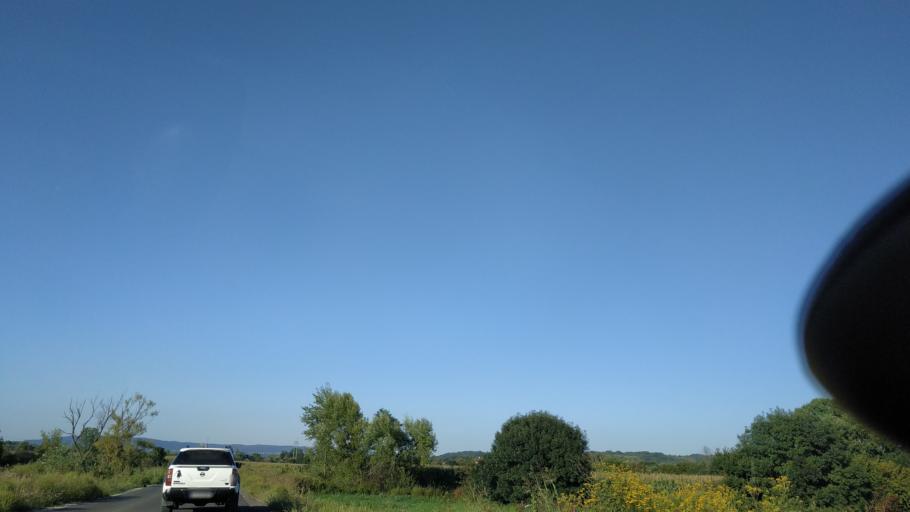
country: RS
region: Central Serbia
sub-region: Rasinski Okrug
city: Krusevac
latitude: 43.5194
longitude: 21.3314
